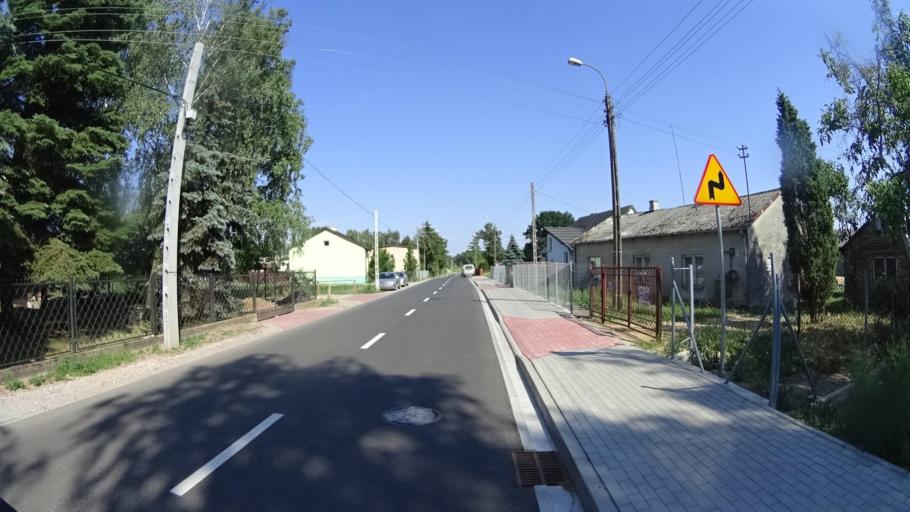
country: PL
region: Masovian Voivodeship
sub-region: Powiat warszawski zachodni
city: Blonie
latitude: 52.1663
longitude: 20.6272
